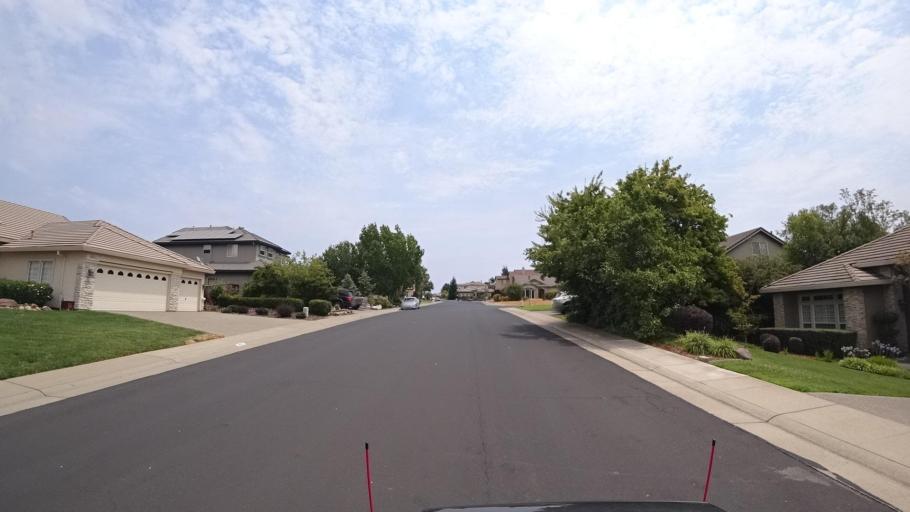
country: US
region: California
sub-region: Placer County
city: Rocklin
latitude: 38.7772
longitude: -121.2118
